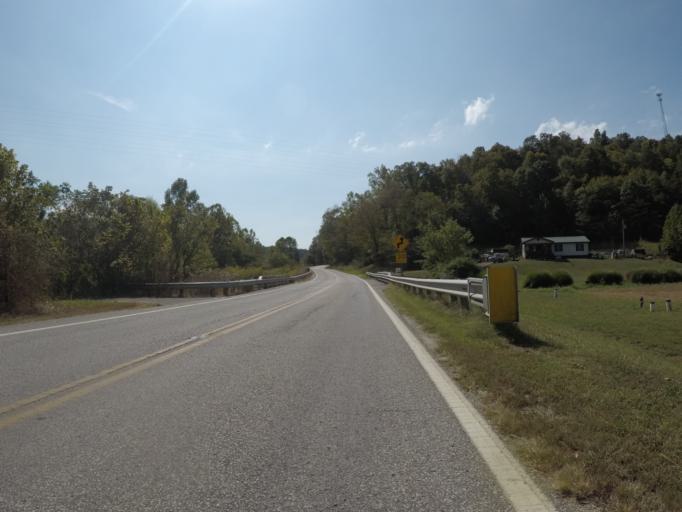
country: US
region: West Virginia
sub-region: Cabell County
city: Lesage
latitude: 38.5559
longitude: -82.3918
